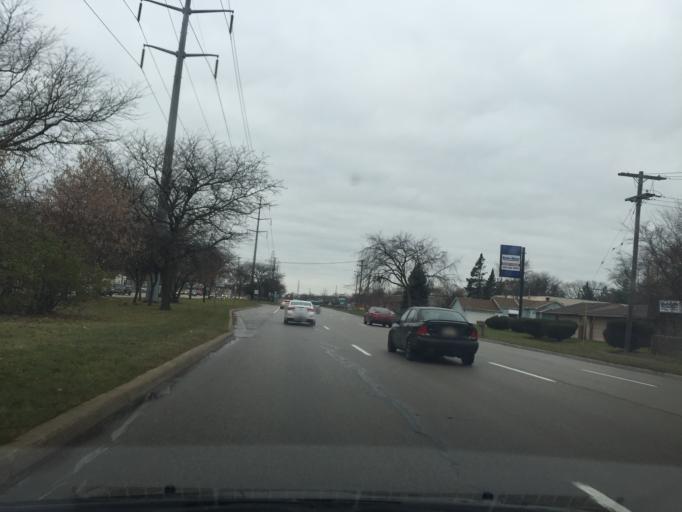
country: US
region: Michigan
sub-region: Wayne County
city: Redford
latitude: 42.4424
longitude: -83.3120
